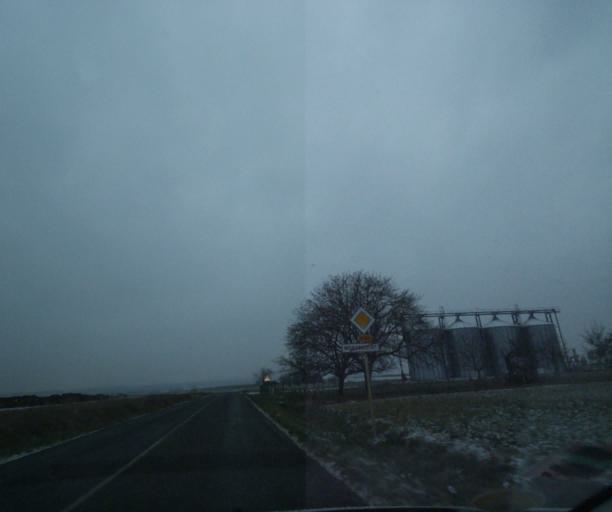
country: FR
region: Champagne-Ardenne
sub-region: Departement de la Haute-Marne
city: Wassy
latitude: 48.4305
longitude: 4.9990
